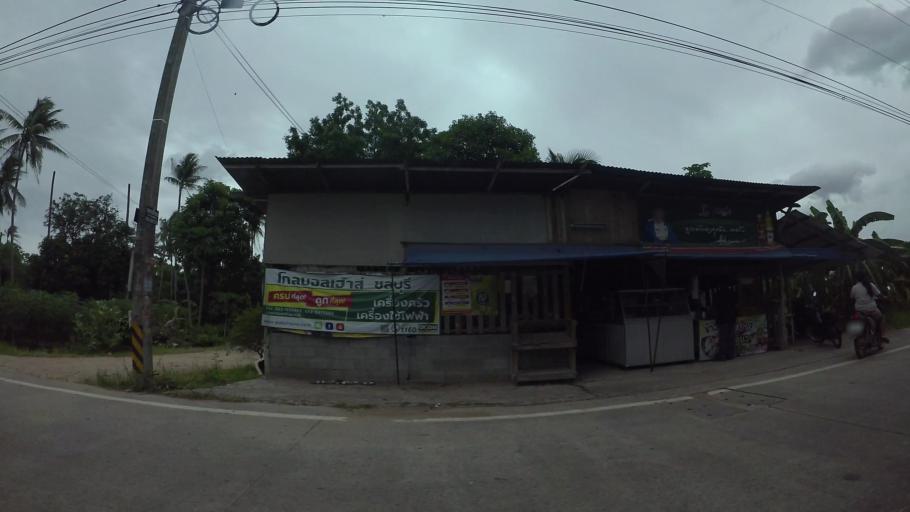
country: TH
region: Chon Buri
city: Si Racha
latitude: 13.1771
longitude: 100.9769
